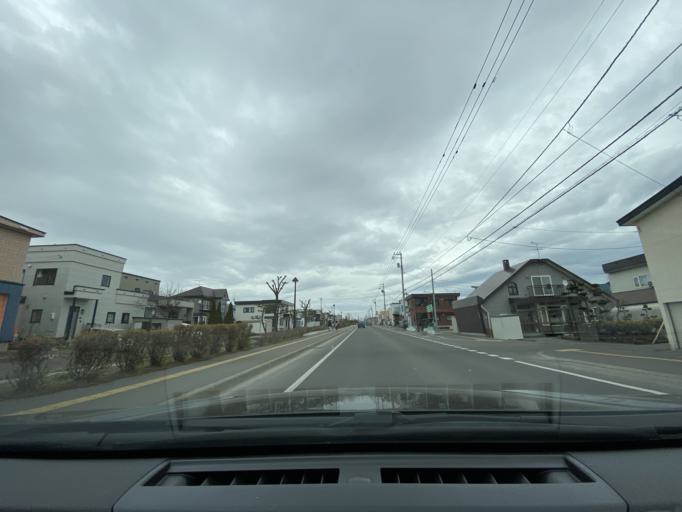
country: JP
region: Hokkaido
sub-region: Asahikawa-shi
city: Asahikawa
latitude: 43.7914
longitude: 142.4150
